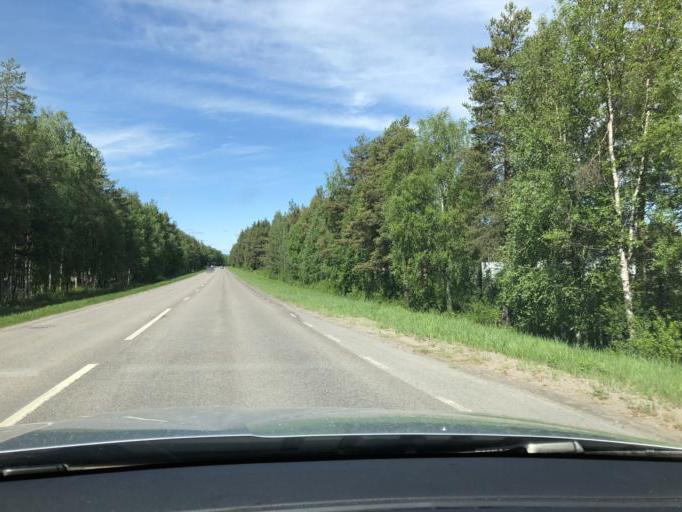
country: SE
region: Norrbotten
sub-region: Pitea Kommun
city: Bergsviken
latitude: 65.3313
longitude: 21.4231
